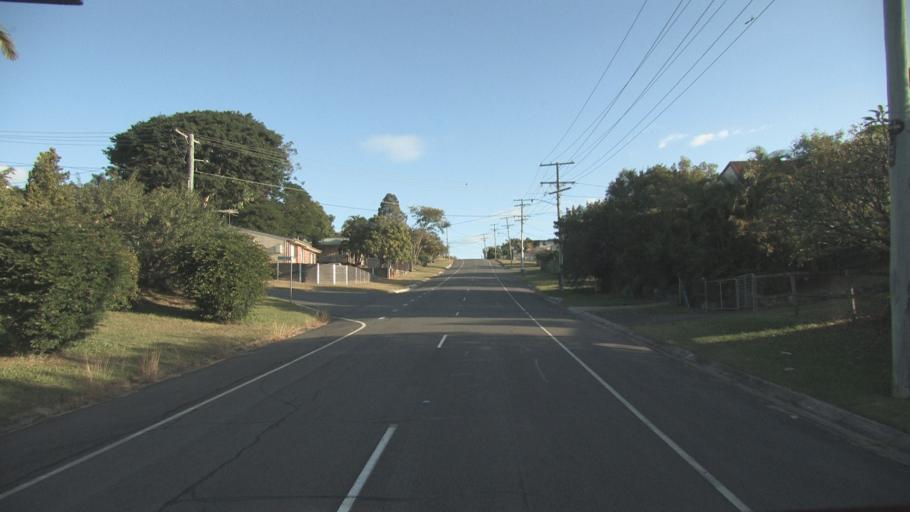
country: AU
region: Queensland
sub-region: Logan
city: Beenleigh
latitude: -27.7065
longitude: 153.1775
